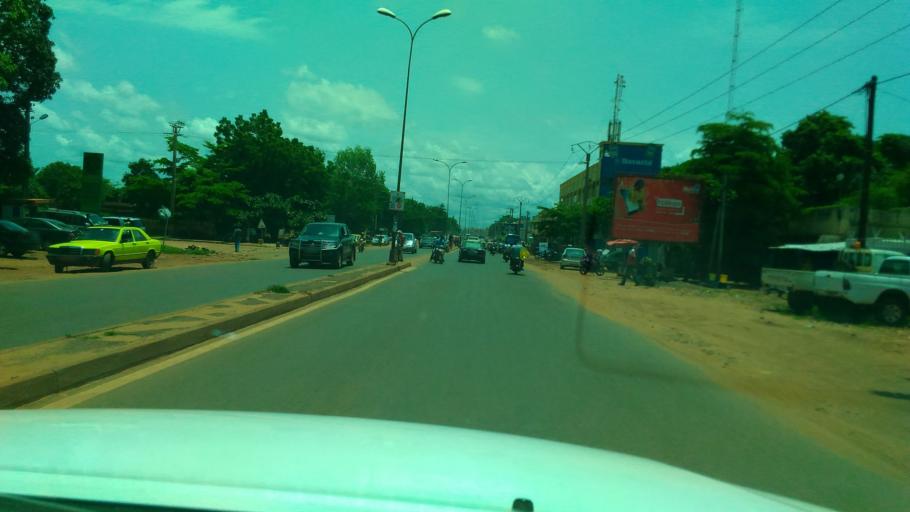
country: ML
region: Bamako
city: Bamako
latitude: 12.6630
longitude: -7.9499
